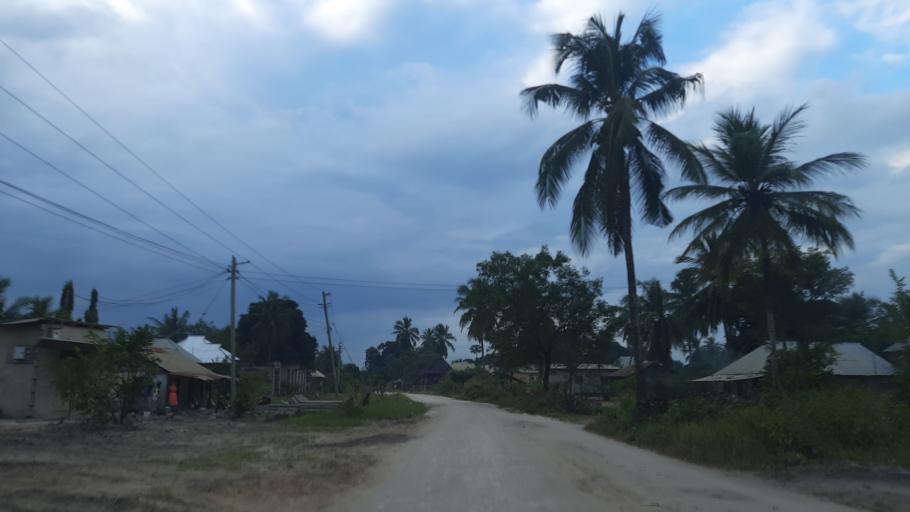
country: TZ
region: Pwani
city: Bagamoyo
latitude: -6.5124
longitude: 38.9307
